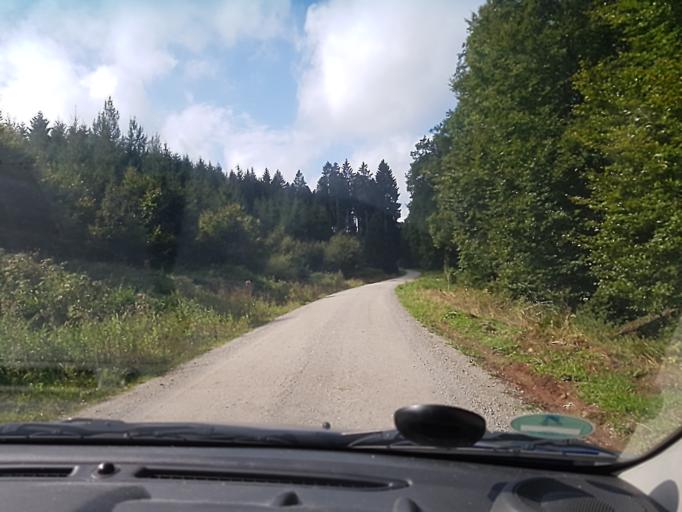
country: DE
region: Lower Saxony
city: Uslar
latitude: 51.7334
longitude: 9.5964
